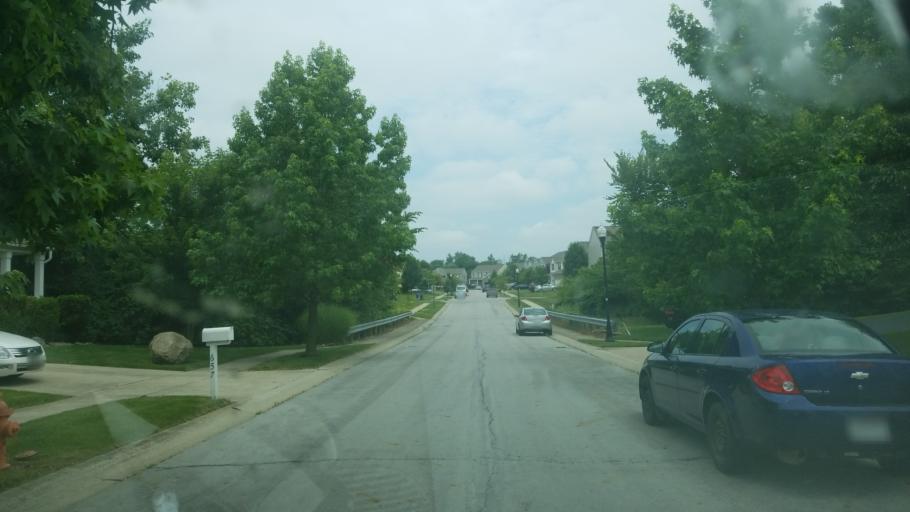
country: US
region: Ohio
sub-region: Franklin County
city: Reynoldsburg
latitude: 39.9998
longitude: -82.7817
